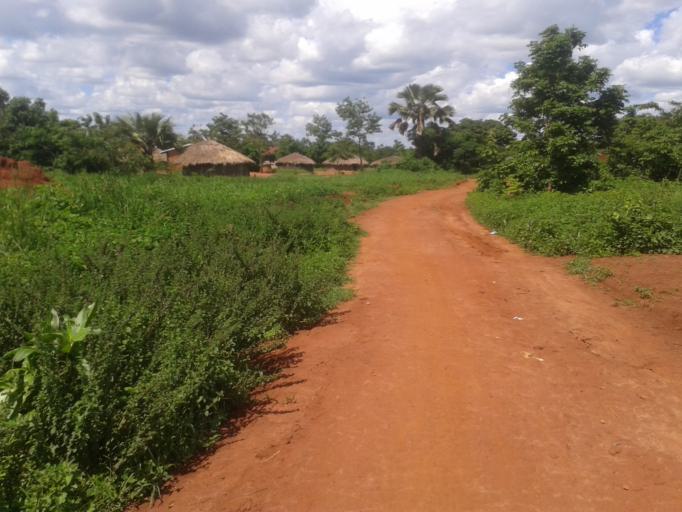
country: UG
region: Northern Region
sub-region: Gulu District
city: Gulu
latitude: 2.7585
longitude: 32.3305
